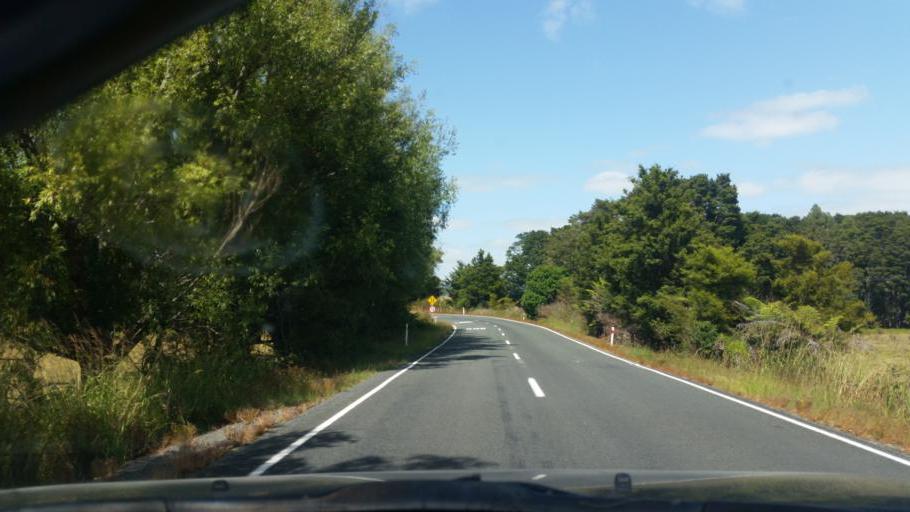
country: NZ
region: Northland
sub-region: Whangarei
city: Ruakaka
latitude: -35.9936
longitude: 174.2936
